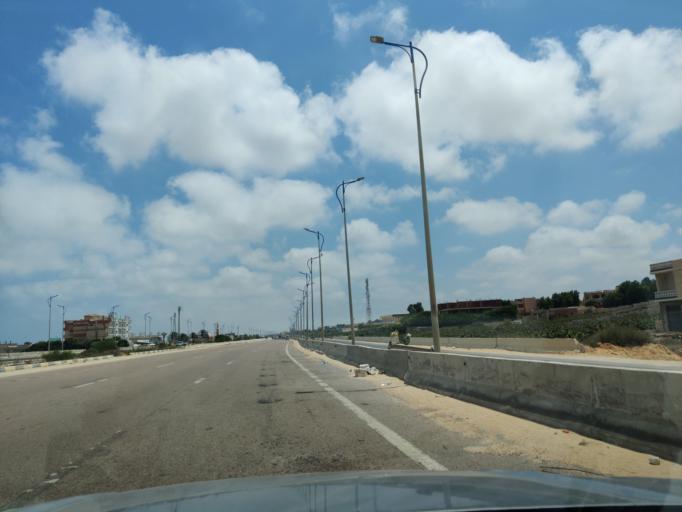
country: EG
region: Alexandria
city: Alexandria
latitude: 30.9649
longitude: 29.5519
